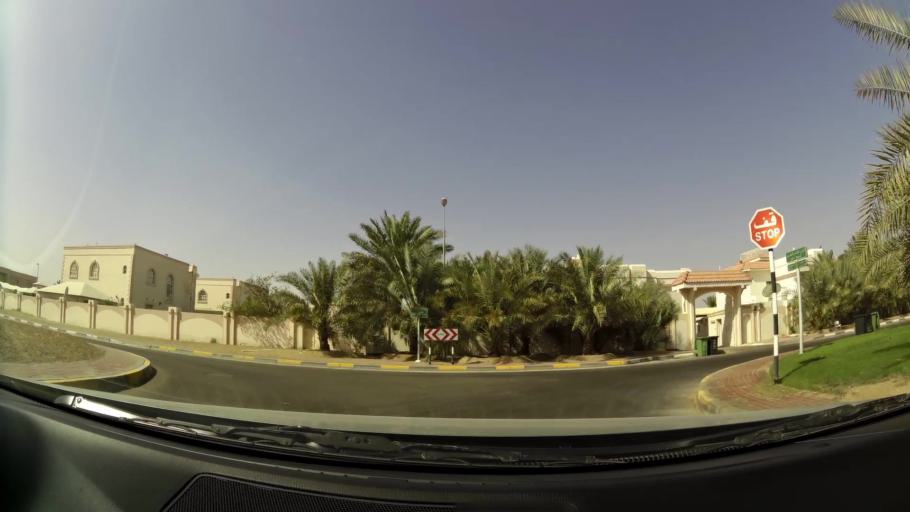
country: OM
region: Al Buraimi
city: Al Buraymi
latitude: 24.3063
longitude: 55.8028
